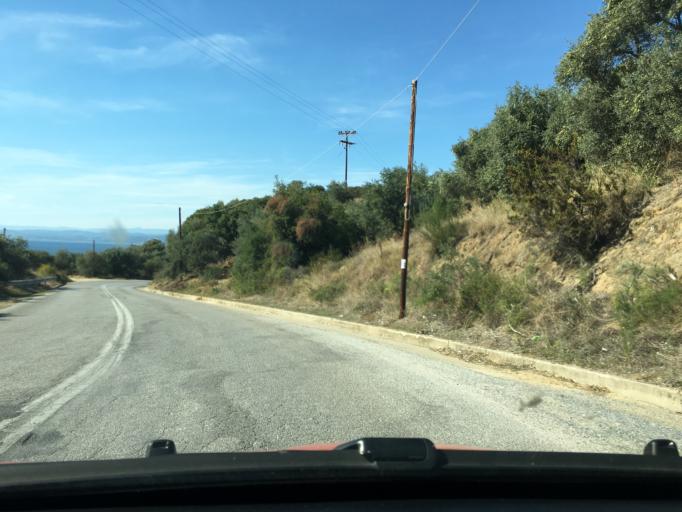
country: GR
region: Central Macedonia
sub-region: Nomos Chalkidikis
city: Ouranoupolis
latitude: 40.3364
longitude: 23.9726
